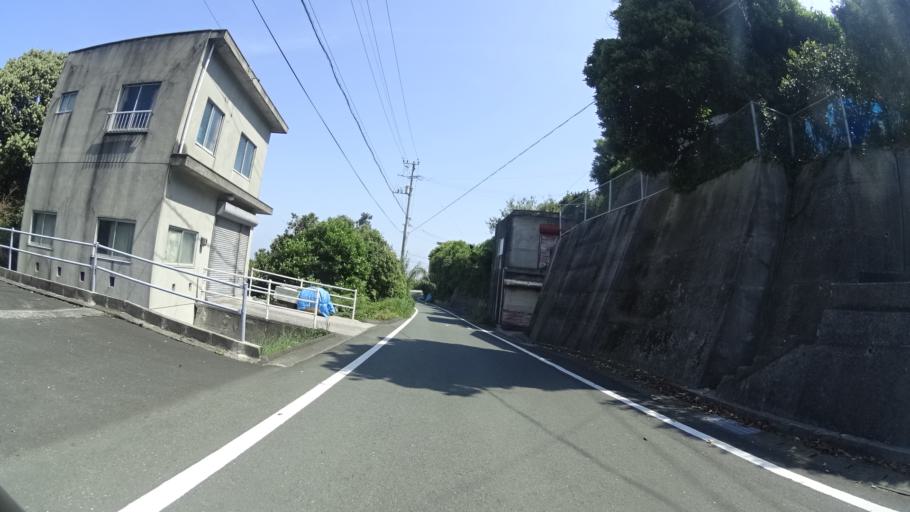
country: JP
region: Ehime
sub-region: Nishiuwa-gun
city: Ikata-cho
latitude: 33.3729
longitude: 132.0539
